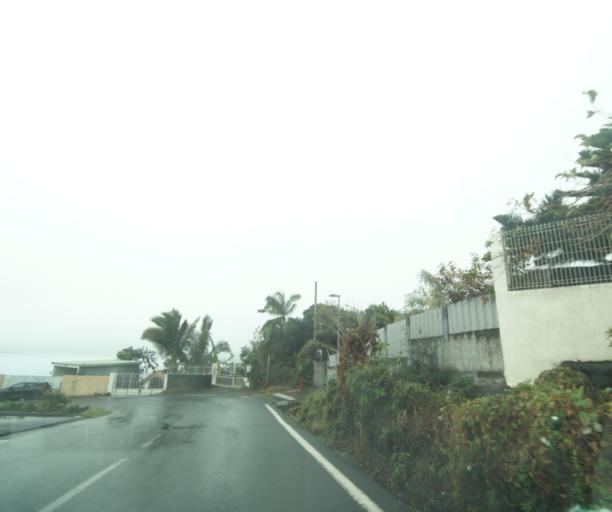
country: RE
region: Reunion
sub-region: Reunion
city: Saint-Paul
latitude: -21.0276
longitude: 55.2863
